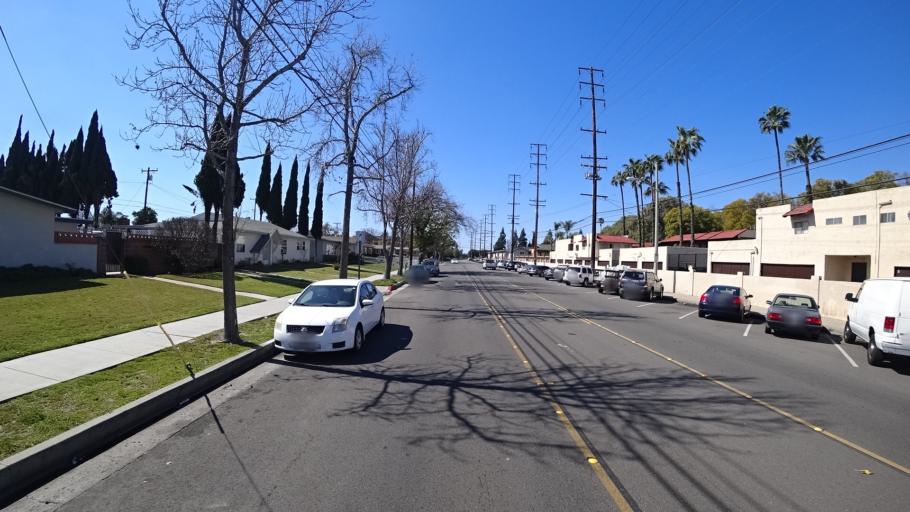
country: US
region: California
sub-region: Orange County
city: Anaheim
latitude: 33.8397
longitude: -117.9444
